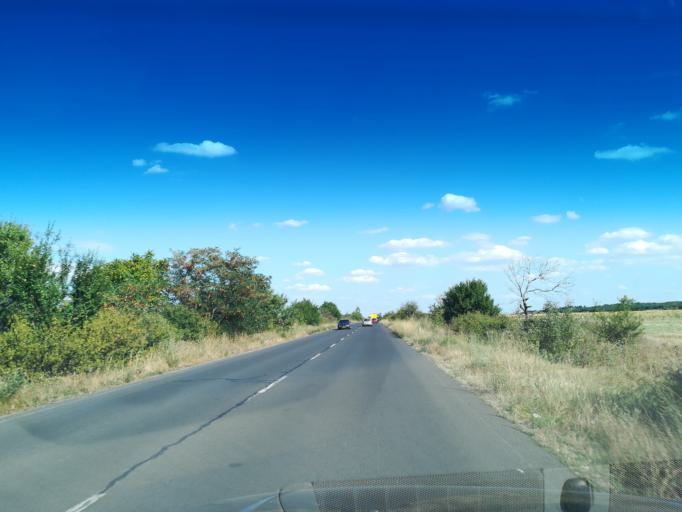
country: BG
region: Stara Zagora
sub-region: Obshtina Chirpan
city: Chirpan
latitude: 42.0650
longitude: 25.2299
